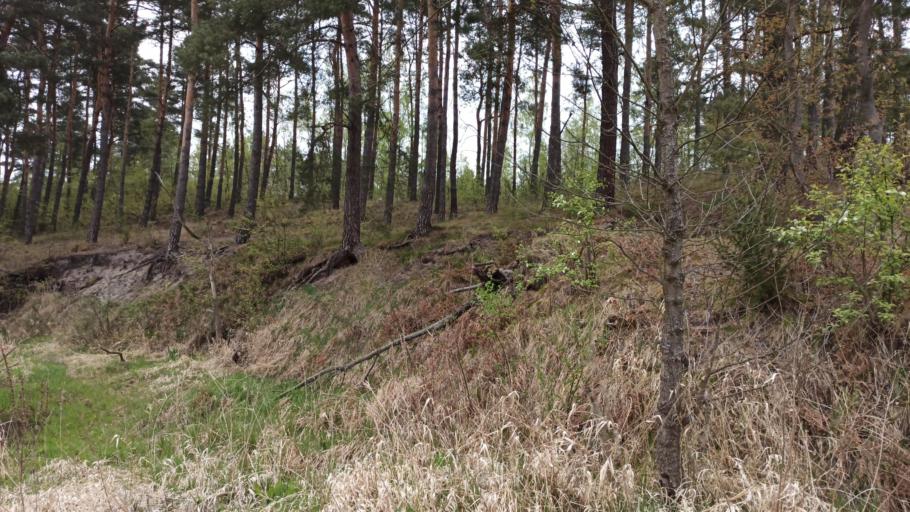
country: PL
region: Lodz Voivodeship
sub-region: Powiat skierniewicki
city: Kaweczyn Nowy
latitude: 51.9430
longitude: 20.2822
